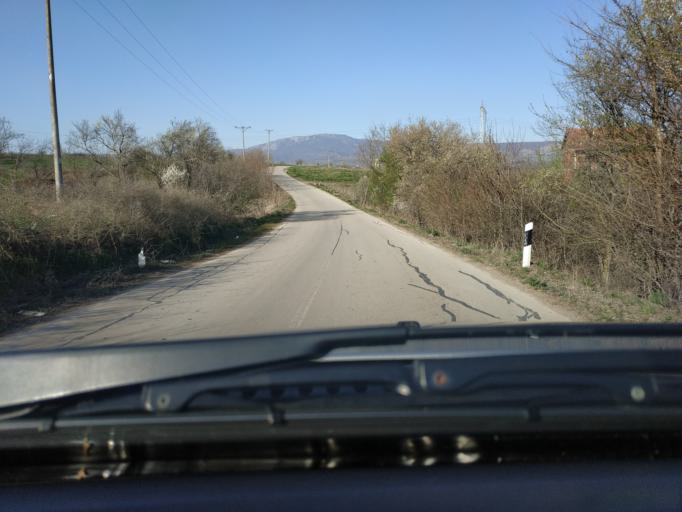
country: RS
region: Central Serbia
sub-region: Nisavski Okrug
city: Aleksinac
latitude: 43.4986
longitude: 21.7881
